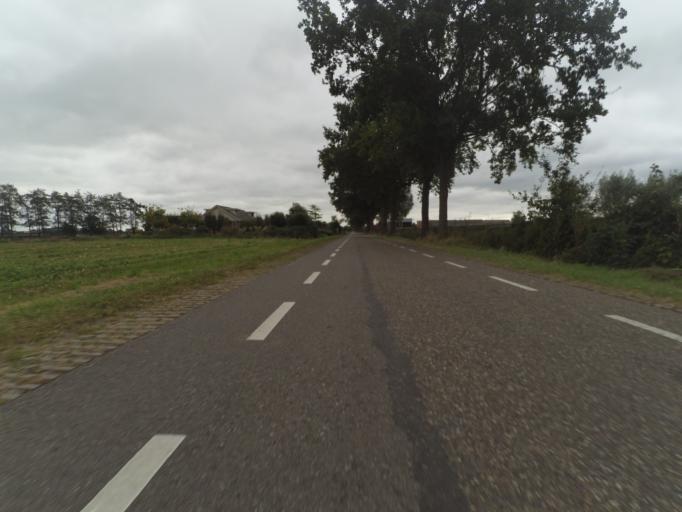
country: NL
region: Utrecht
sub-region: Gemeente Utrechtse Heuvelrug
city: Overberg
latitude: 52.0576
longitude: 5.5196
